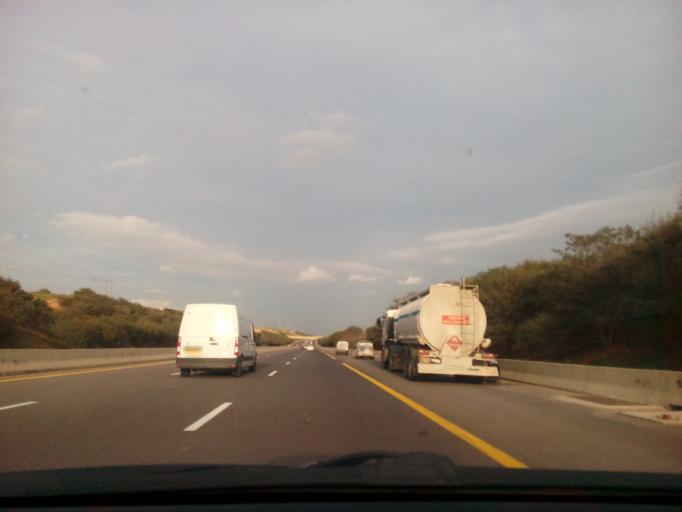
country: DZ
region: Relizane
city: Relizane
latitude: 35.7443
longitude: 0.3439
